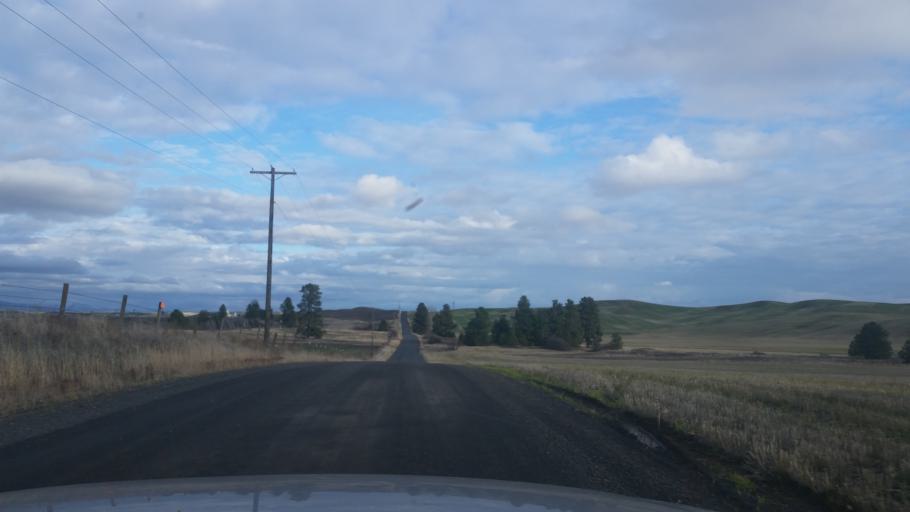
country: US
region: Washington
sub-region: Spokane County
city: Cheney
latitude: 47.4272
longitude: -117.4200
